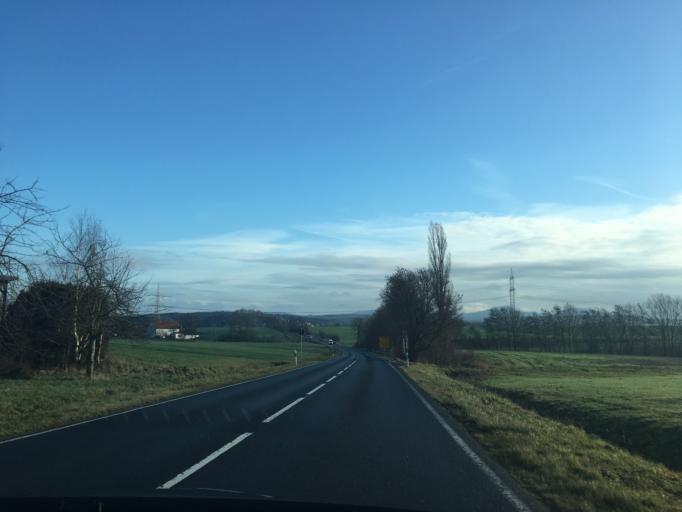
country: DE
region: Hesse
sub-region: Regierungsbezirk Kassel
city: Petersberg
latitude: 50.5640
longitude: 9.7430
